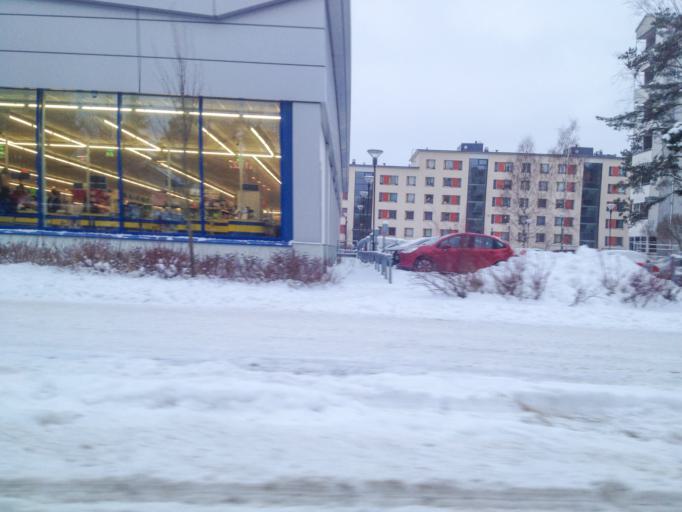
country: FI
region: Uusimaa
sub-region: Helsinki
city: Vantaa
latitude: 60.2146
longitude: 25.1337
